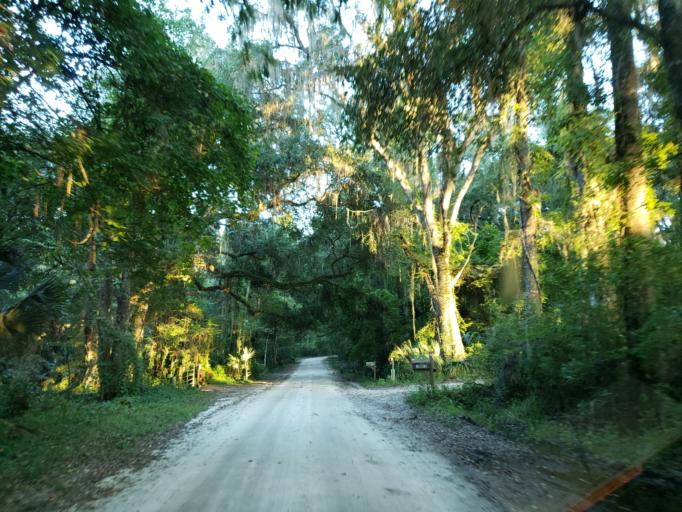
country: US
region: Florida
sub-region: Alachua County
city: Gainesville
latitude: 29.4882
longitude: -82.2781
